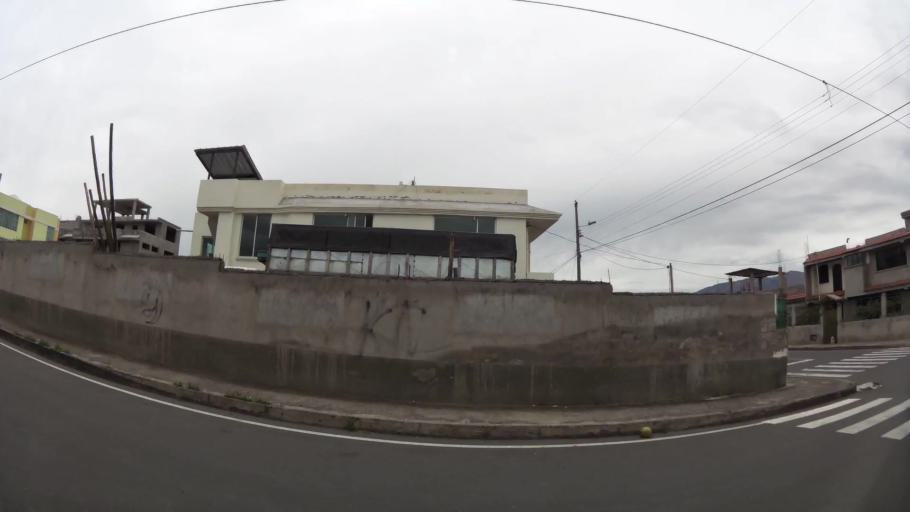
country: EC
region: Cotopaxi
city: San Miguel de Salcedo
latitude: -1.0366
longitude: -78.5876
